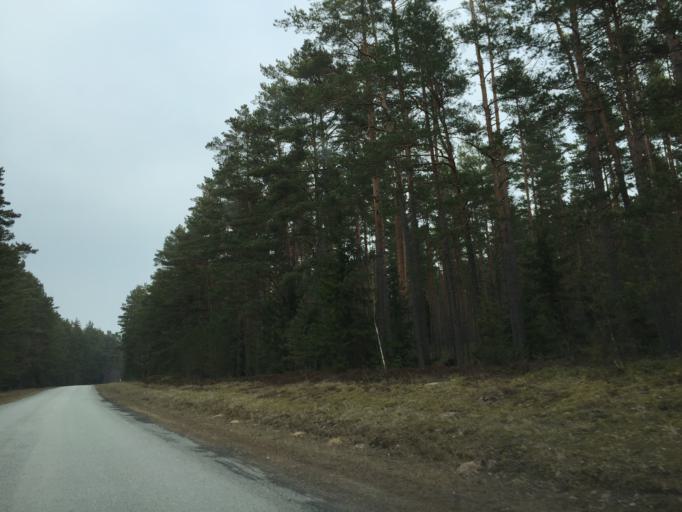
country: LV
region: Salacgrivas
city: Ainazi
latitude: 57.9819
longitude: 24.4167
